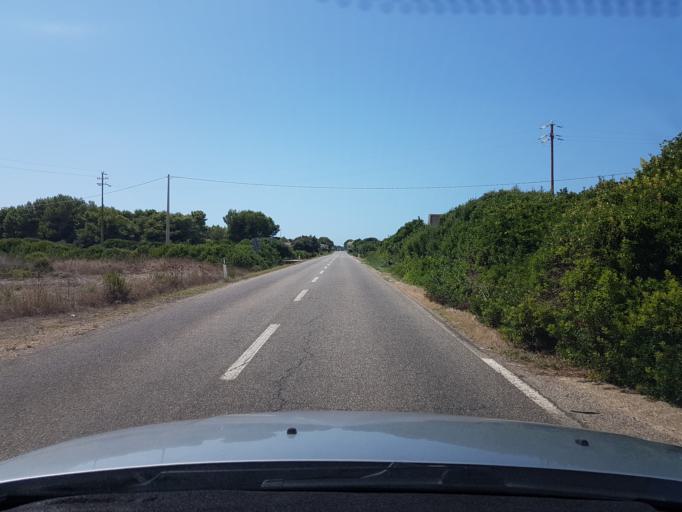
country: IT
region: Sardinia
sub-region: Provincia di Oristano
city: Riola Sardo
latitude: 40.0223
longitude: 8.4504
